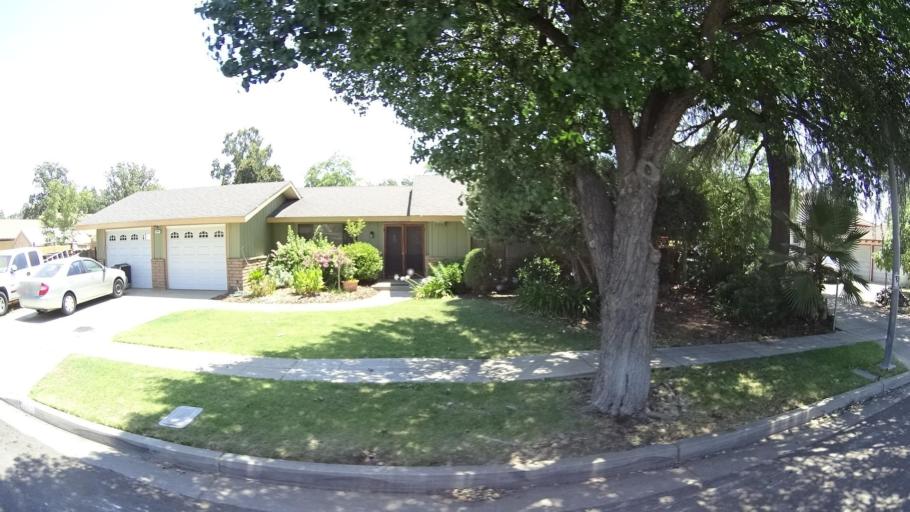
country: US
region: California
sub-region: Fresno County
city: Sunnyside
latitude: 36.7616
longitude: -119.7238
